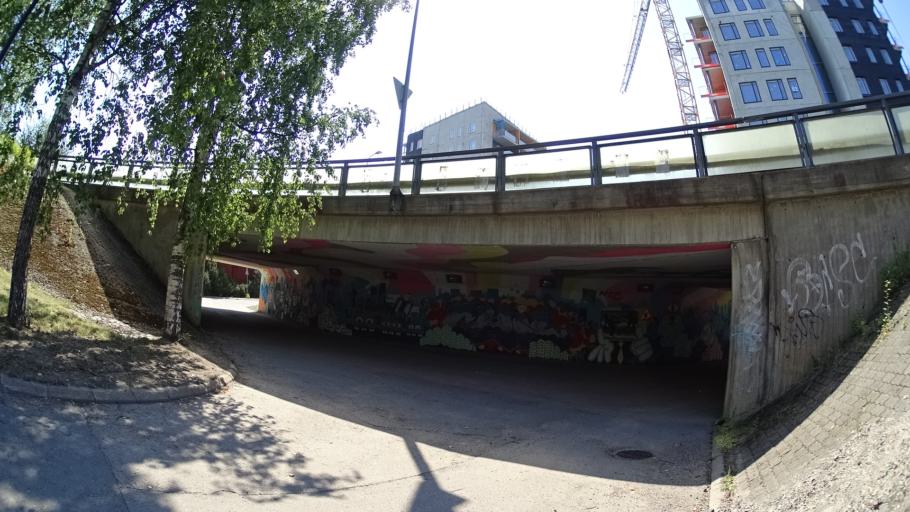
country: FI
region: Uusimaa
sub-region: Helsinki
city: Kerava
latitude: 60.3518
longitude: 25.0733
